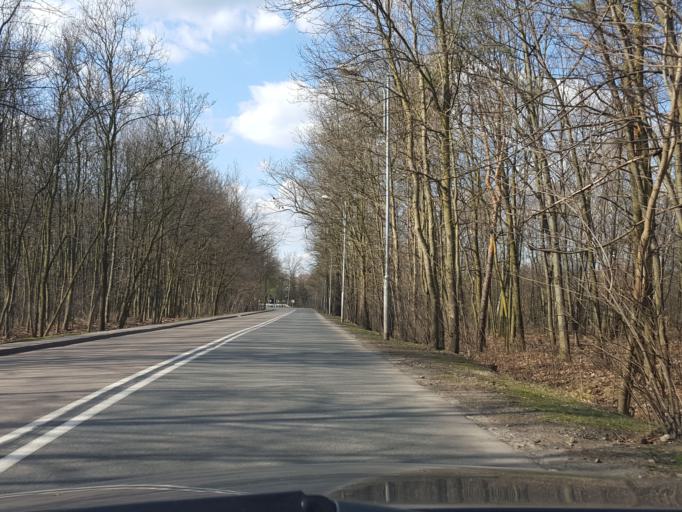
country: PL
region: Silesian Voivodeship
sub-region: Ruda Slaska
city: Ruda Slaska
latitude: 50.2350
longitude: 18.8571
